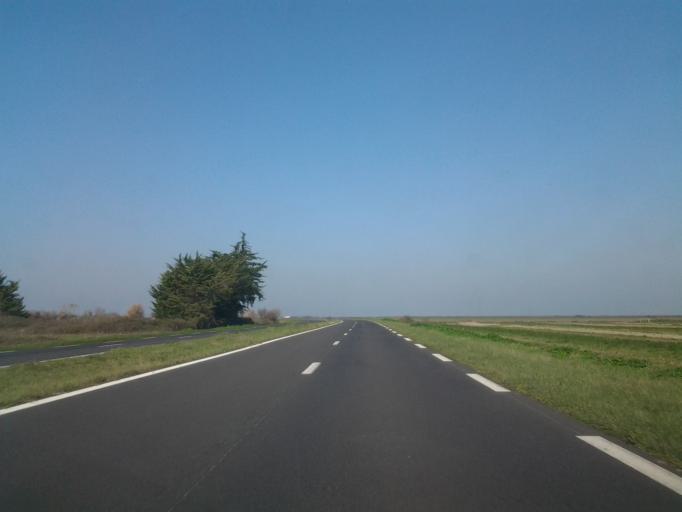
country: FR
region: Pays de la Loire
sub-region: Departement de la Vendee
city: Barbatre
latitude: 46.9466
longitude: -2.1733
